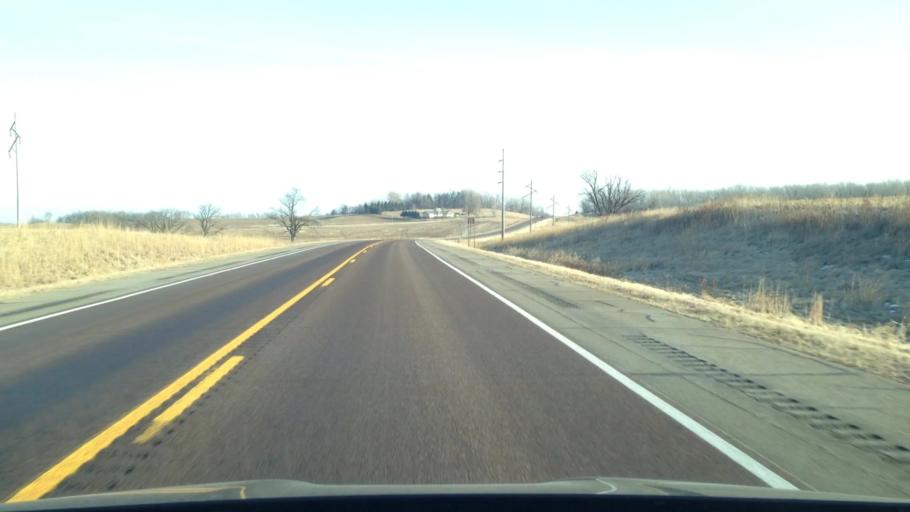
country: US
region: Minnesota
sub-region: Goodhue County
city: Goodhue
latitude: 44.4359
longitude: -92.6133
